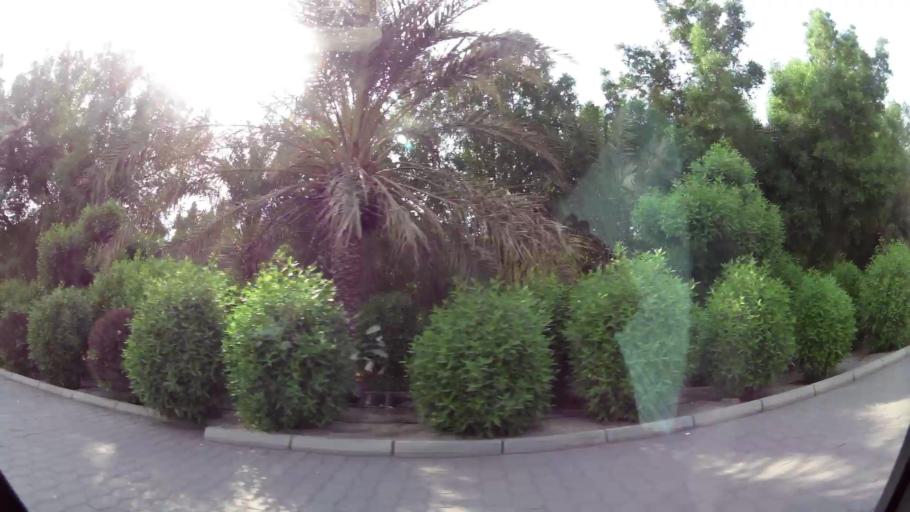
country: KW
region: Al Farwaniyah
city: Al Farwaniyah
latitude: 29.2921
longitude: 47.9664
